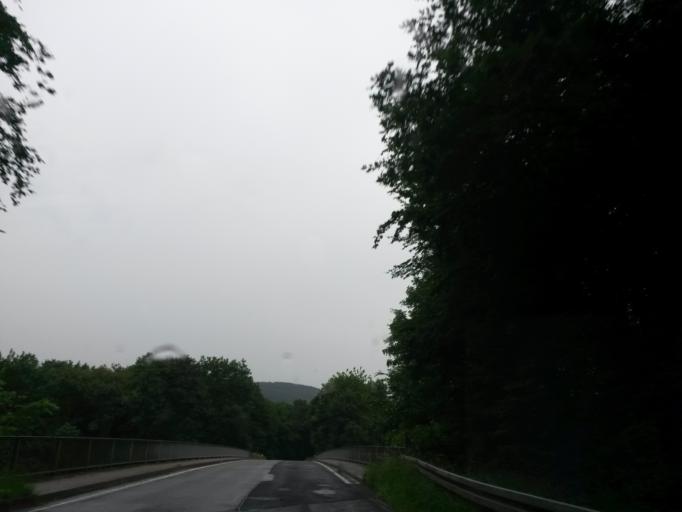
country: DE
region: North Rhine-Westphalia
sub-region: Regierungsbezirk Koln
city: Engelskirchen
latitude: 50.9660
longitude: 7.3616
